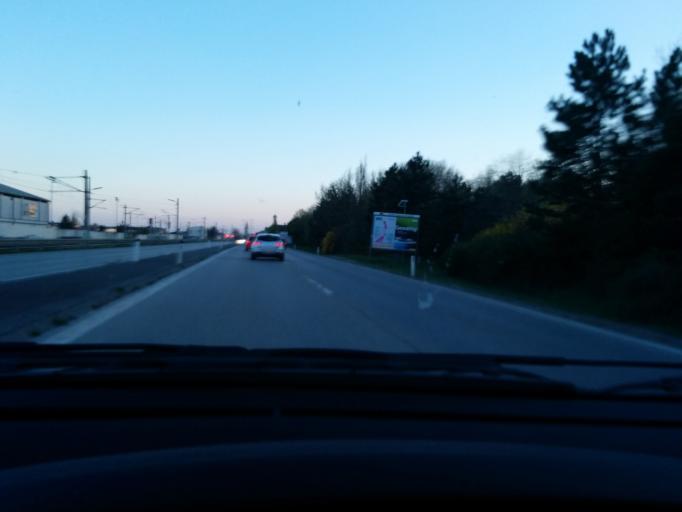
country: AT
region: Lower Austria
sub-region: Politischer Bezirk Modling
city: Wiener Neudorf
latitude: 48.0909
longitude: 16.3139
